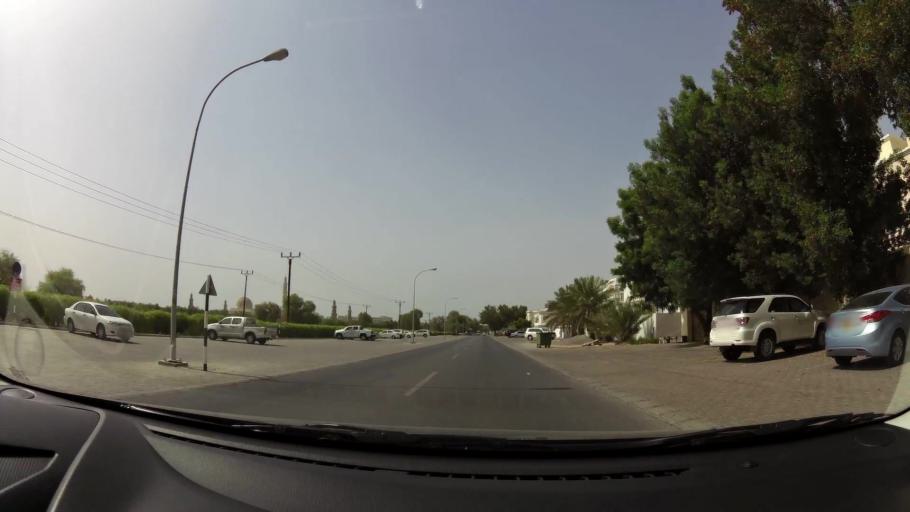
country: OM
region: Muhafazat Masqat
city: Bawshar
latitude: 23.5778
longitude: 58.3912
